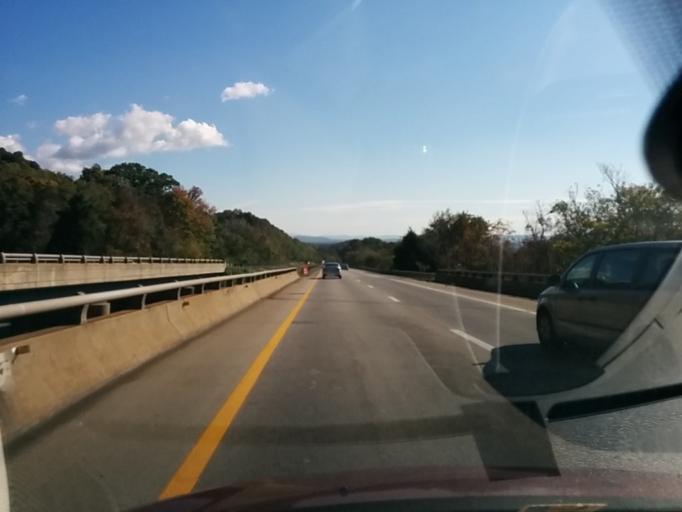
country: US
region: Virginia
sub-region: Albemarle County
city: Crozet
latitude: 38.0467
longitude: -78.7879
